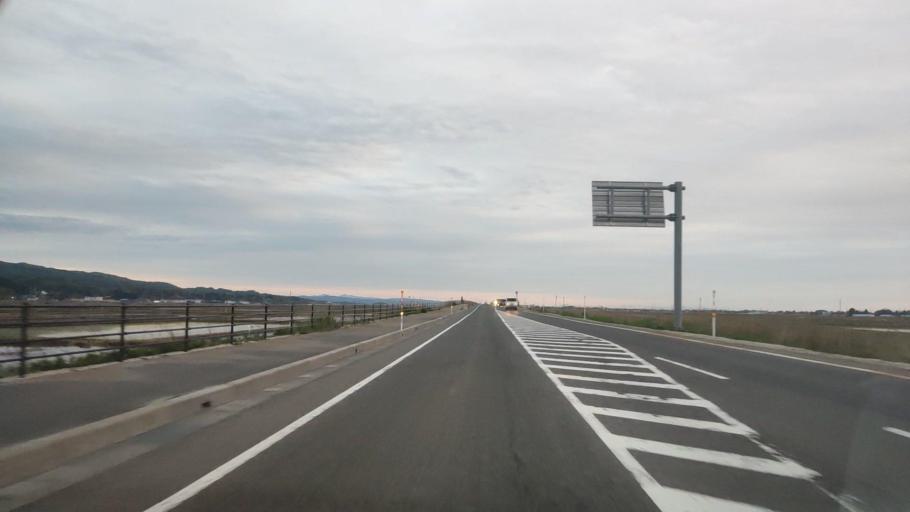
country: JP
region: Niigata
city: Niitsu-honcho
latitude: 37.7506
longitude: 139.0874
